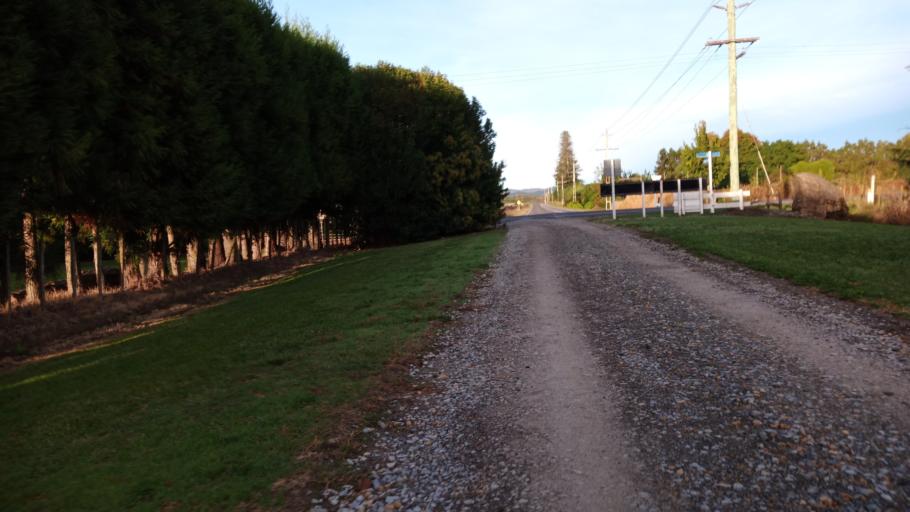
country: NZ
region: Gisborne
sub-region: Gisborne District
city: Gisborne
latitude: -38.6480
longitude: 177.9473
